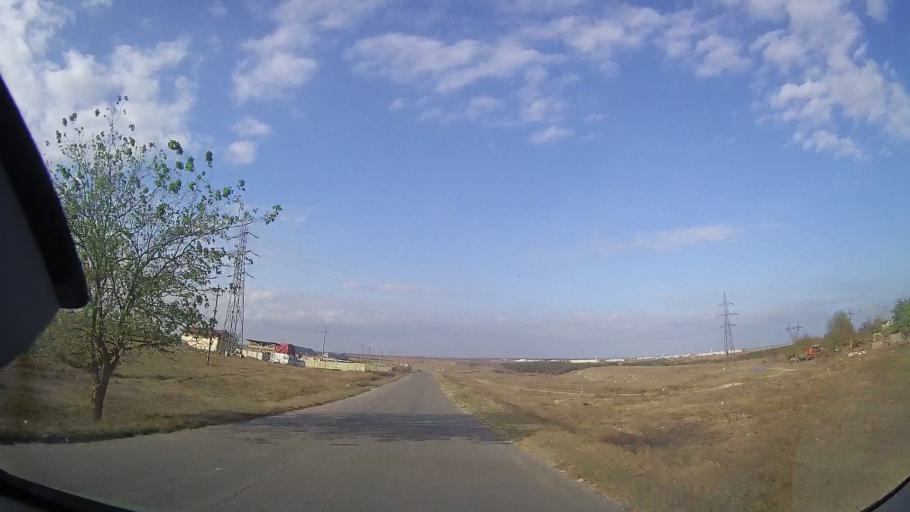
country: RO
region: Constanta
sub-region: Comuna Limanu
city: Limanu
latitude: 43.8022
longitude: 28.5219
